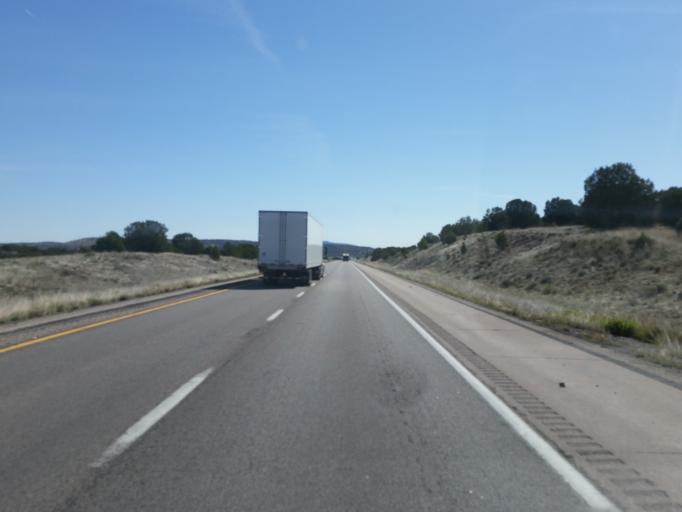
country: US
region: Arizona
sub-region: Mohave County
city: Peach Springs
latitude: 35.2210
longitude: -113.2448
